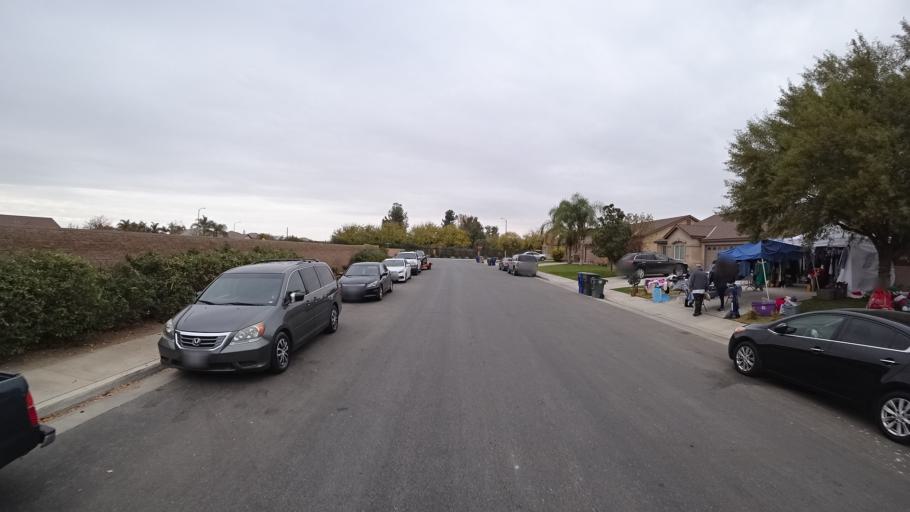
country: US
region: California
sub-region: Kern County
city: Greenfield
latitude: 35.2892
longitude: -119.0314
